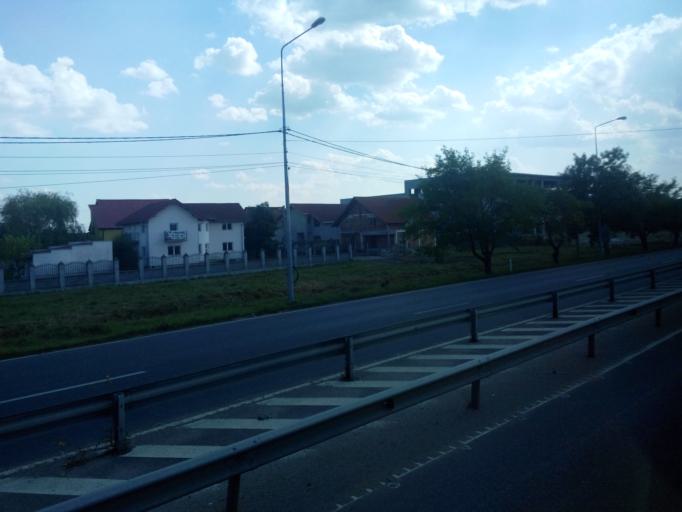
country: RO
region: Timis
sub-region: Comuna Ghiroda
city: Ghiroda
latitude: 45.7760
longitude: 21.3050
